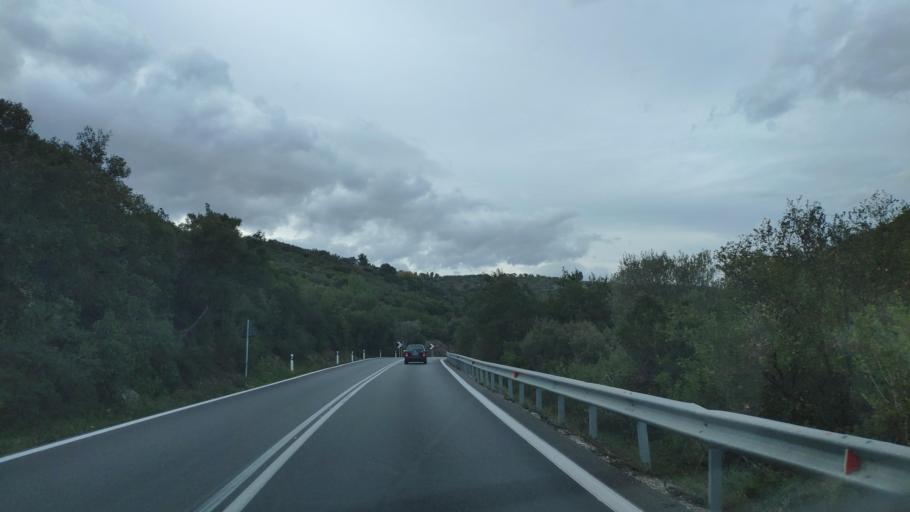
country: GR
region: Peloponnese
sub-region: Nomos Korinthias
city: Ayios Vasilios
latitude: 37.7686
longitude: 22.7274
